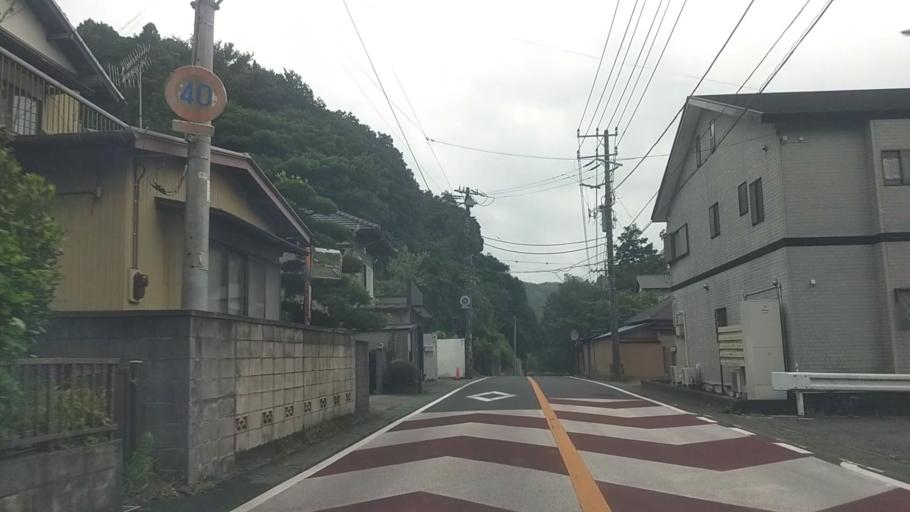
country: JP
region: Chiba
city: Kisarazu
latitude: 35.2934
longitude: 140.0799
